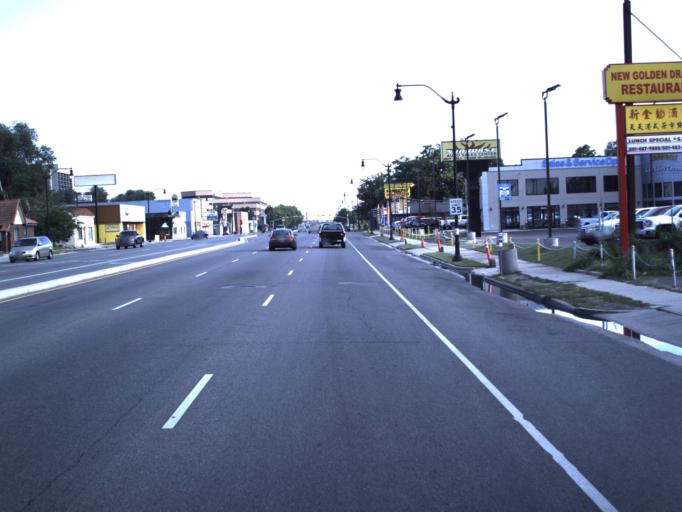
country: US
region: Utah
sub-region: Salt Lake County
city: South Salt Lake
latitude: 40.7329
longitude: -111.8884
